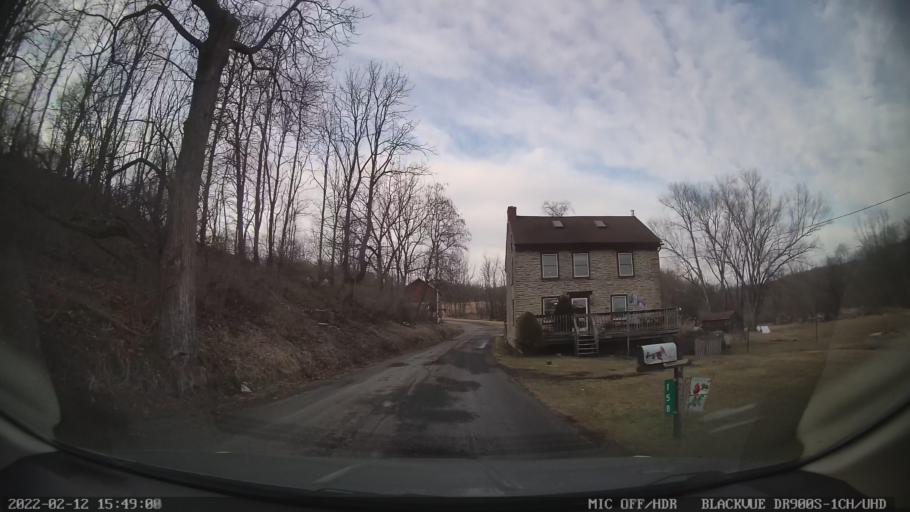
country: US
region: Pennsylvania
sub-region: Berks County
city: Kutztown
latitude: 40.5734
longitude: -75.7481
